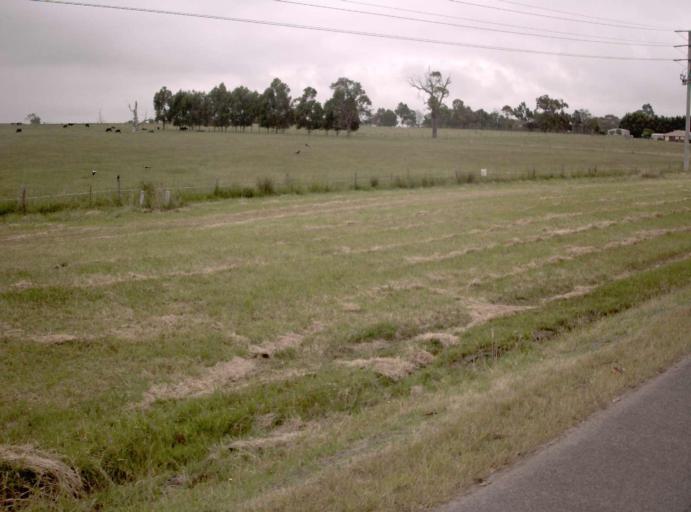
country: AU
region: Victoria
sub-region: Latrobe
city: Morwell
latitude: -38.2536
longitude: 146.4754
